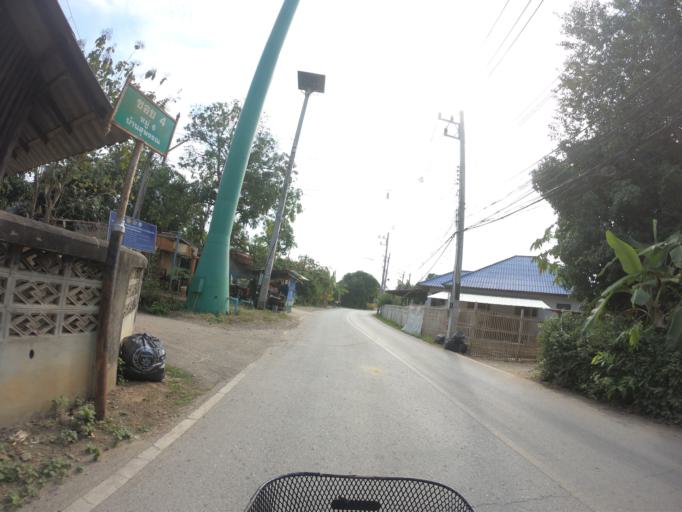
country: TH
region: Chiang Mai
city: Saraphi
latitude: 18.7296
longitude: 99.0622
